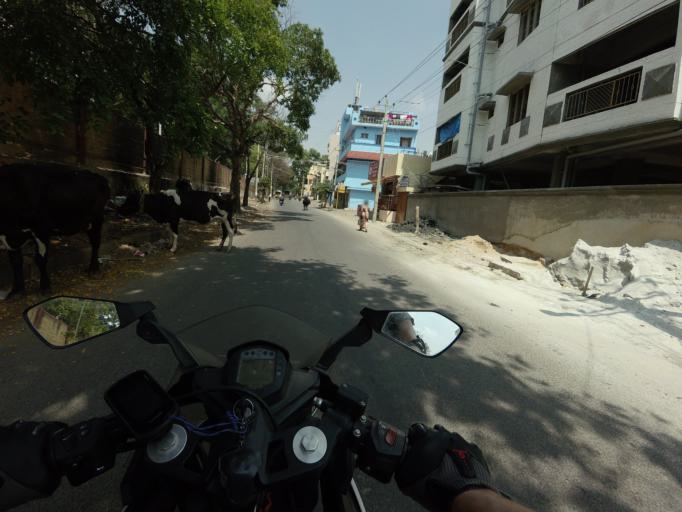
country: IN
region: Karnataka
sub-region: Bangalore Urban
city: Bangalore
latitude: 13.0064
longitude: 77.6433
